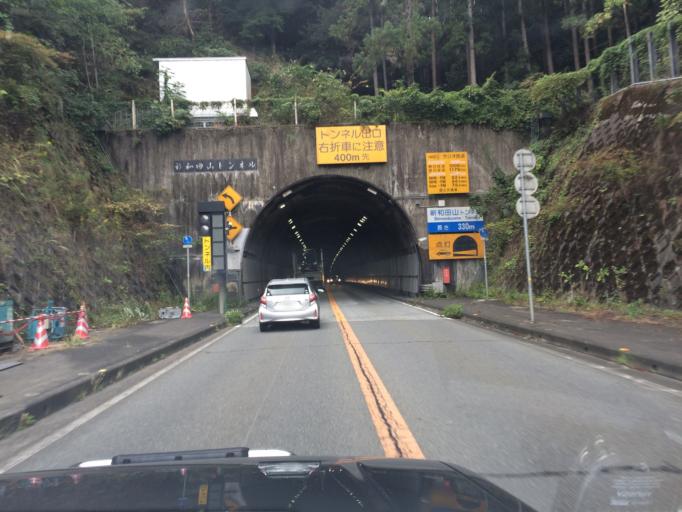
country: JP
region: Hyogo
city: Toyooka
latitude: 35.3365
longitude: 134.8549
